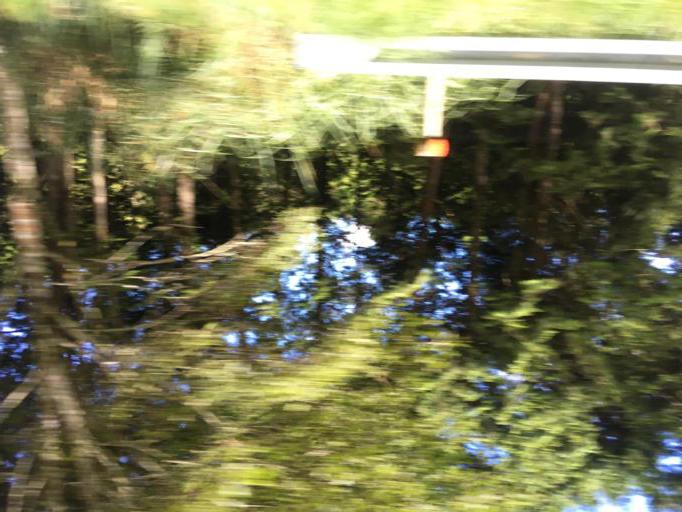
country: TW
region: Taiwan
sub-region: Yilan
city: Yilan
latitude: 24.5137
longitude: 121.5889
